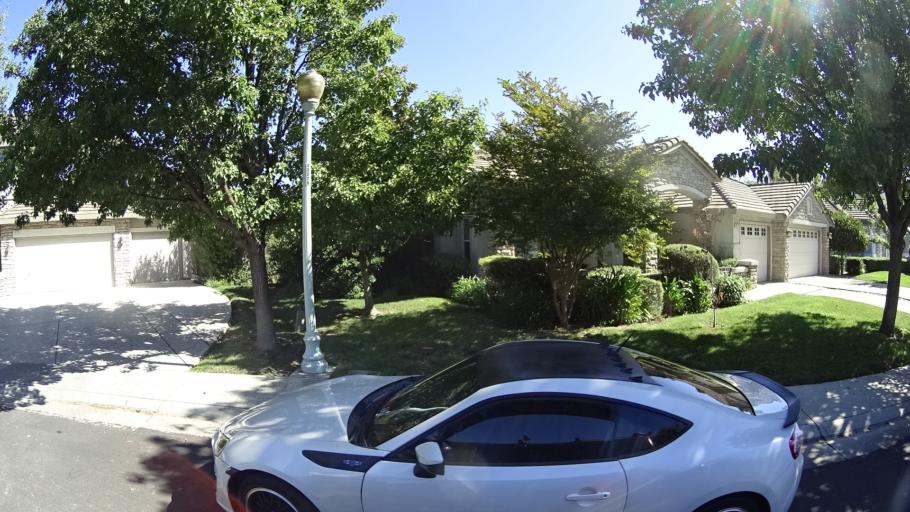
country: US
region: California
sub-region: Sacramento County
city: Laguna
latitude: 38.4205
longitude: -121.4721
